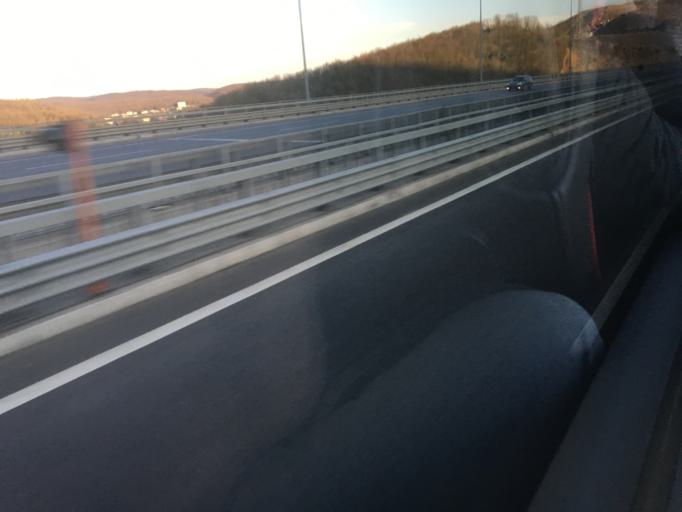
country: TR
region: Istanbul
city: Mahmut Sevket Pasa
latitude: 41.1397
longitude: 29.2852
